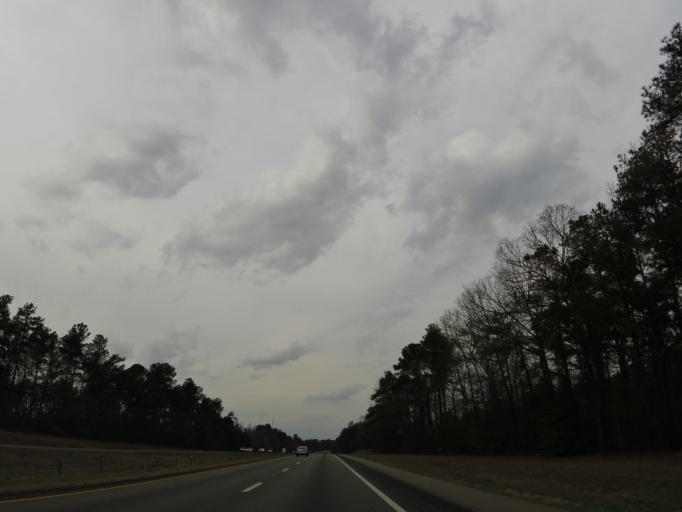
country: US
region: South Carolina
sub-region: Calhoun County
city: Oak Grove
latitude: 33.6846
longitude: -80.9060
